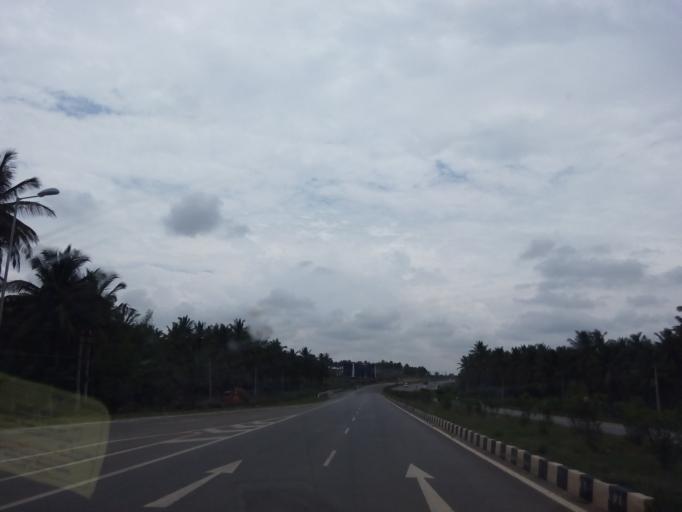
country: IN
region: Karnataka
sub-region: Hassan
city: Channarayapatna
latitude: 12.9759
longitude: 76.3062
